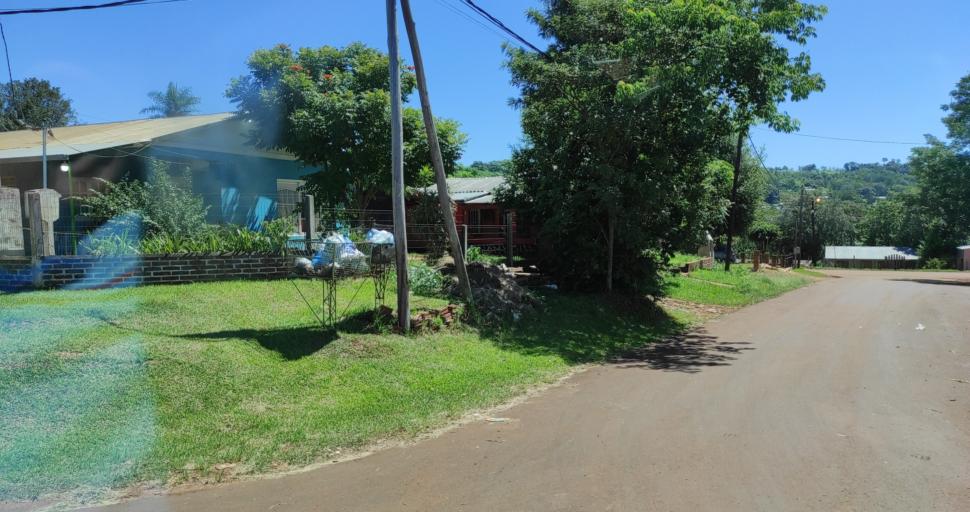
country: AR
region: Misiones
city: El Soberbio
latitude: -27.3014
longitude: -54.1939
